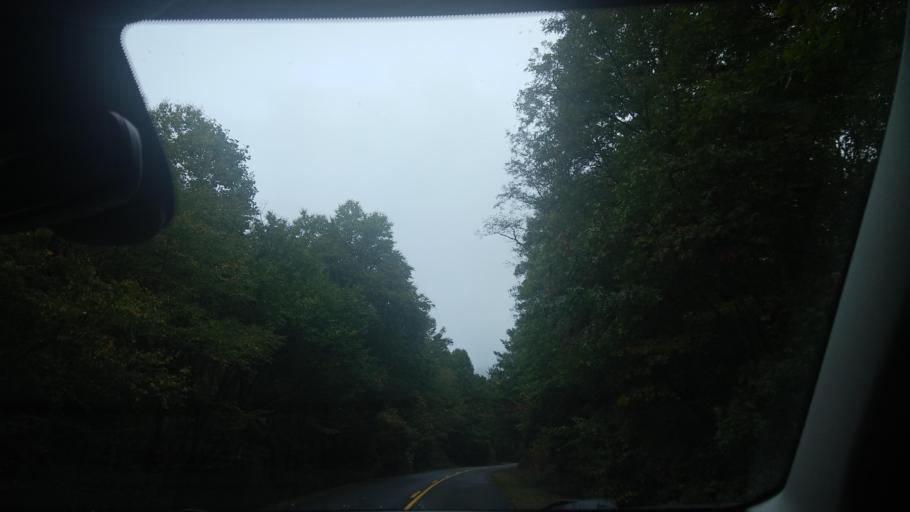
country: US
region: North Carolina
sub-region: Mitchell County
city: Spruce Pine
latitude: 35.9070
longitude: -81.9674
